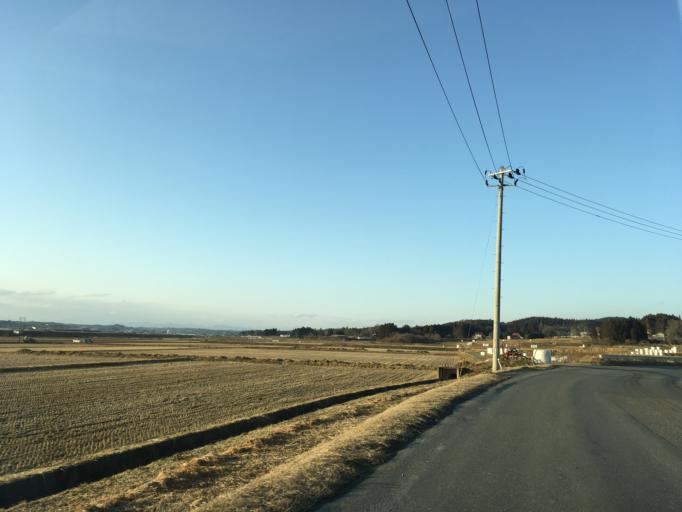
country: JP
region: Iwate
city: Ichinoseki
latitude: 38.8128
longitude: 141.2138
